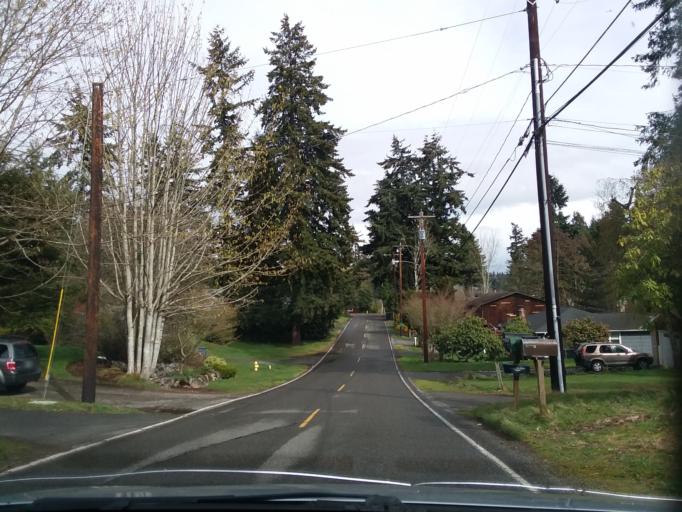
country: US
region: Washington
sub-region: Snohomish County
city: Esperance
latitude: 47.7869
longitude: -122.3374
